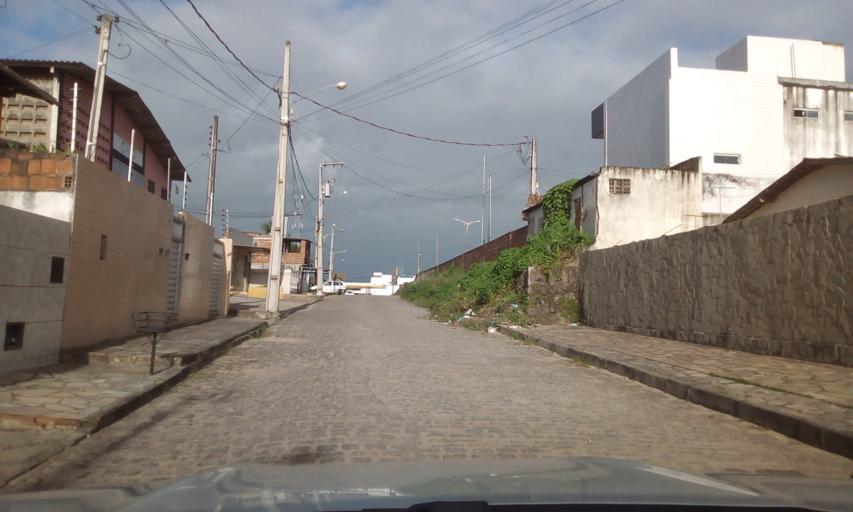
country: BR
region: Paraiba
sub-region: Joao Pessoa
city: Joao Pessoa
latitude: -7.1640
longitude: -34.8516
